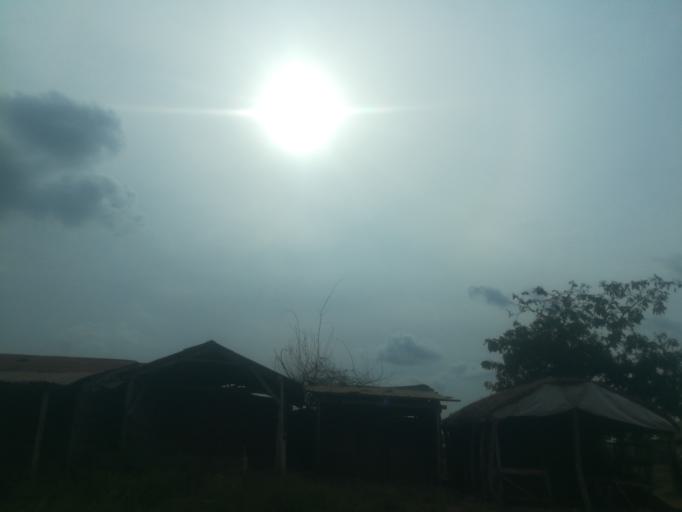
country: NG
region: Ogun
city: Ayetoro
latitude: 7.3138
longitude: 3.0709
